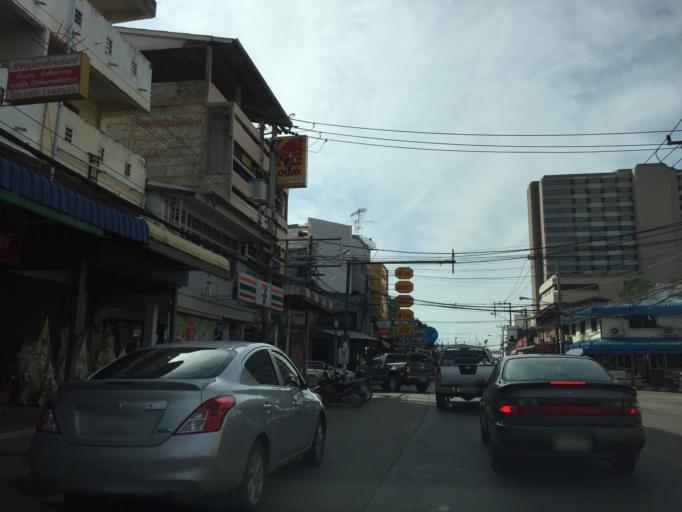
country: TH
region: Phitsanulok
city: Phitsanulok
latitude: 16.8235
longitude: 100.2650
